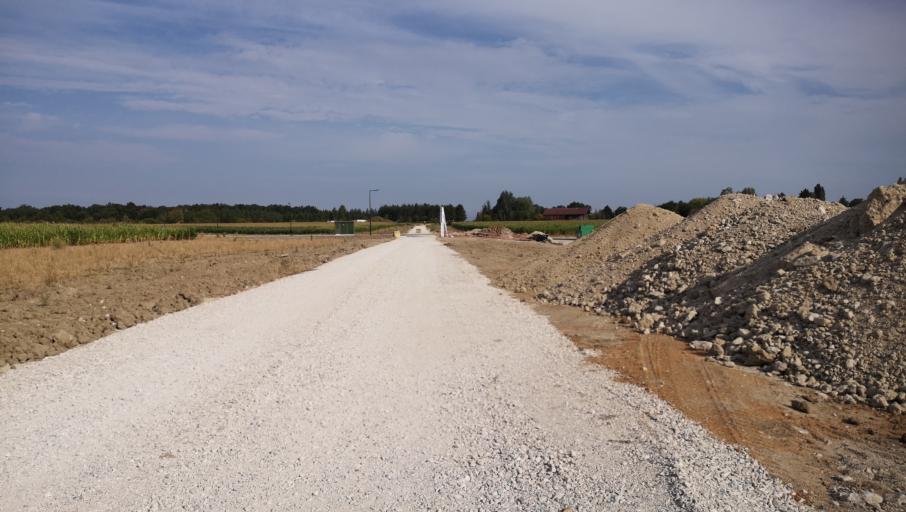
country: FR
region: Centre
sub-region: Departement du Loiret
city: Marigny-les-Usages
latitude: 47.9464
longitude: 2.0143
